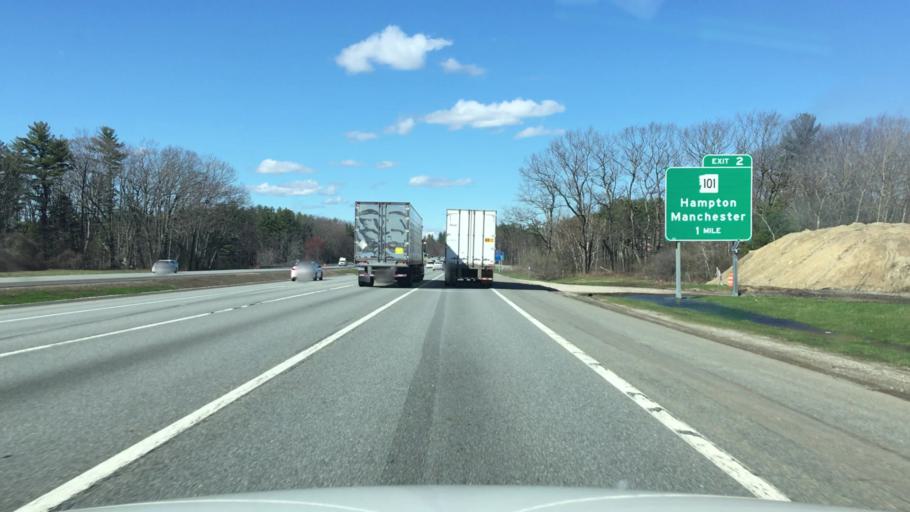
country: US
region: New Hampshire
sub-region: Rockingham County
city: Hampton Falls
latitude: 42.9299
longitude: -70.8644
